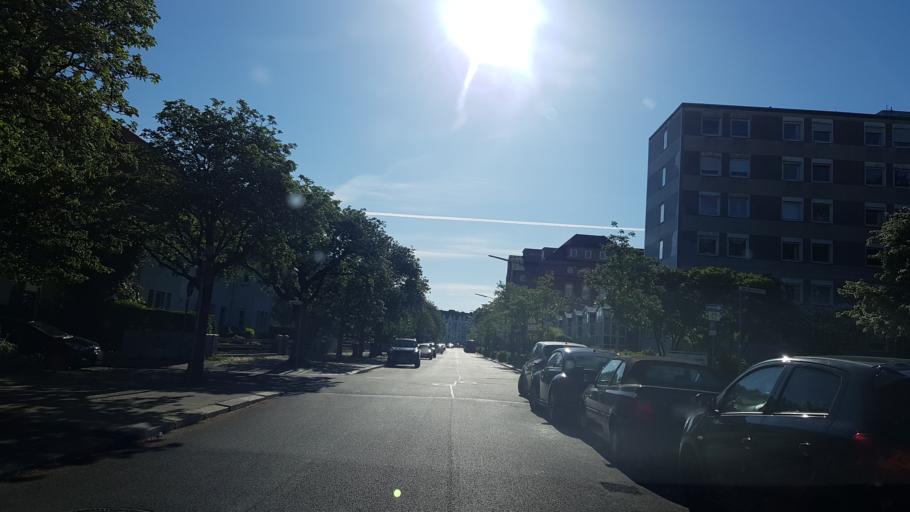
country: DE
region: Bremen
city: Bremerhaven
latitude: 53.5528
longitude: 8.5735
